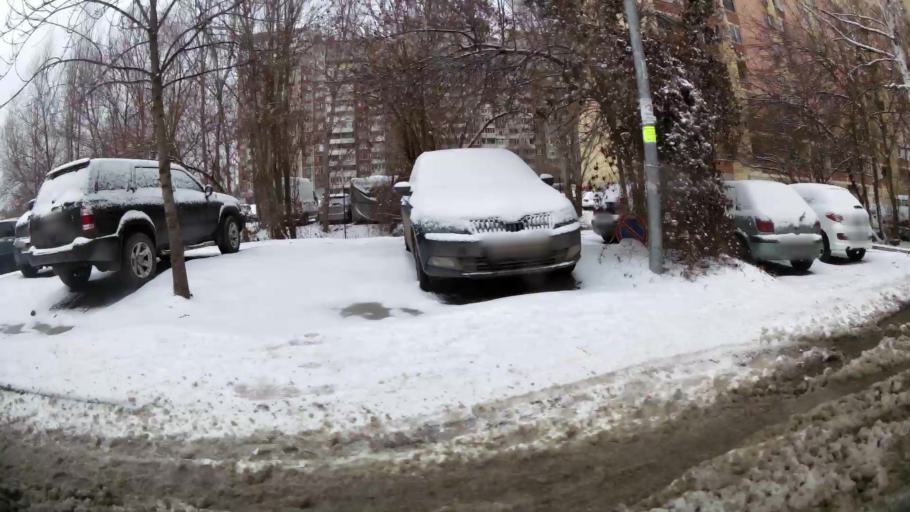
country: BG
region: Sofia-Capital
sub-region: Stolichna Obshtina
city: Sofia
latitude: 42.6966
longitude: 23.3102
